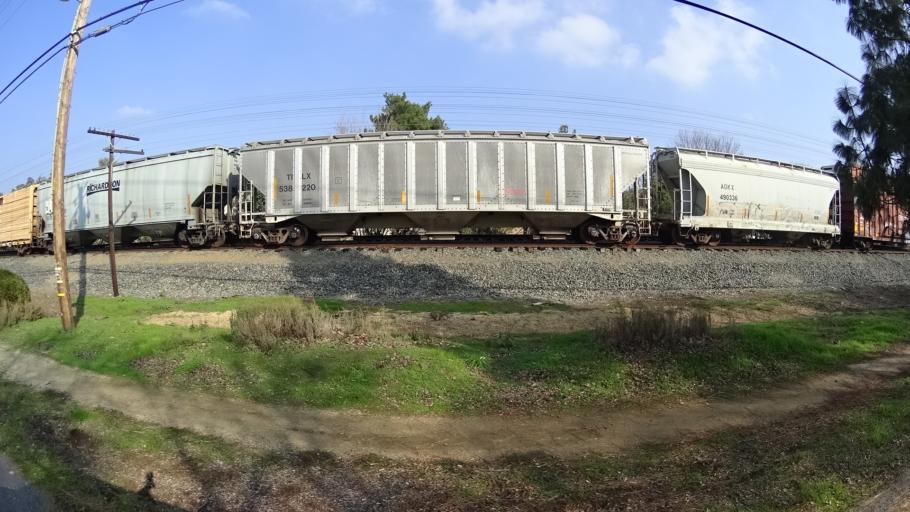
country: US
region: California
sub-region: Yolo County
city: Davis
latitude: 38.5554
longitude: -121.7416
